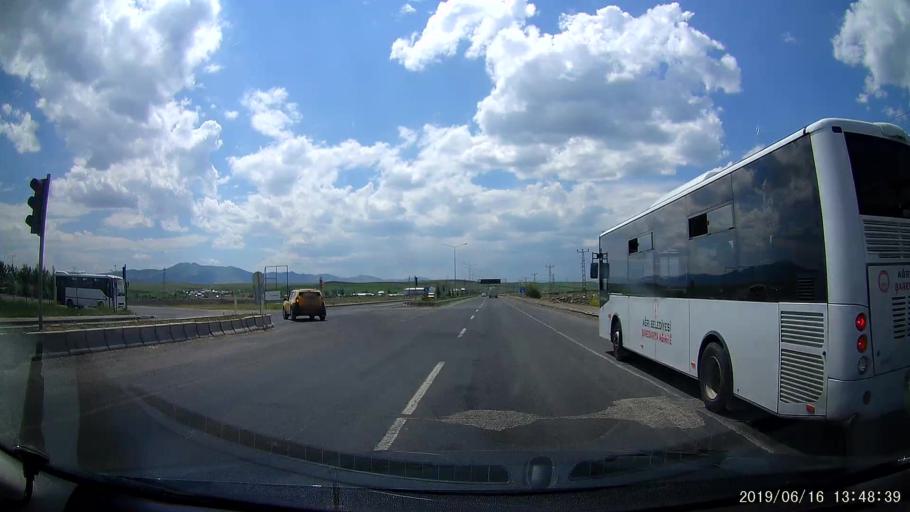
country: TR
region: Agri
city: Agri
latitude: 39.7145
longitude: 43.0033
